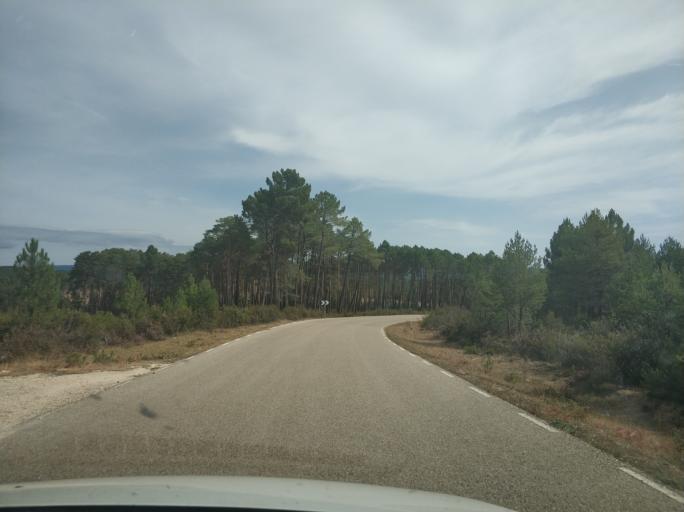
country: ES
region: Castille and Leon
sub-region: Provincia de Soria
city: Navaleno
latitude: 41.8514
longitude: -2.9805
